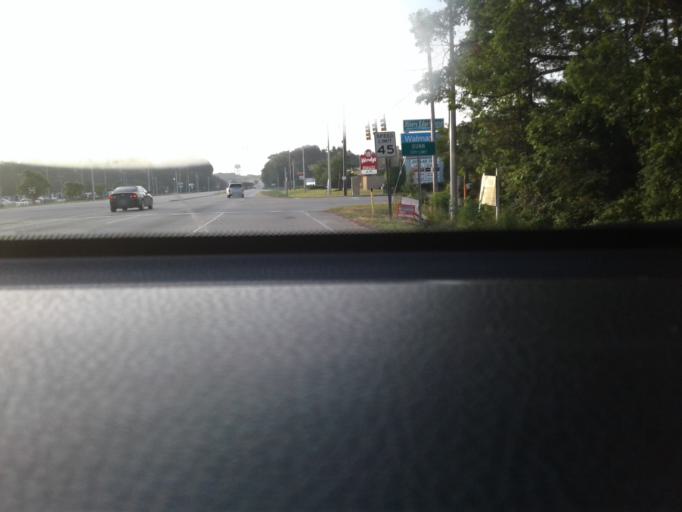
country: US
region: North Carolina
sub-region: Harnett County
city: Erwin
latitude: 35.3242
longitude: -78.6481
